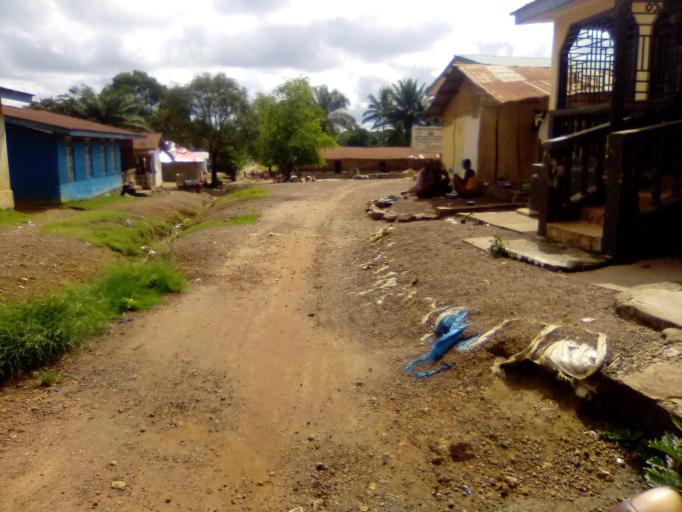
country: SL
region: Southern Province
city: Baoma
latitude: 7.9798
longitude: -11.7263
